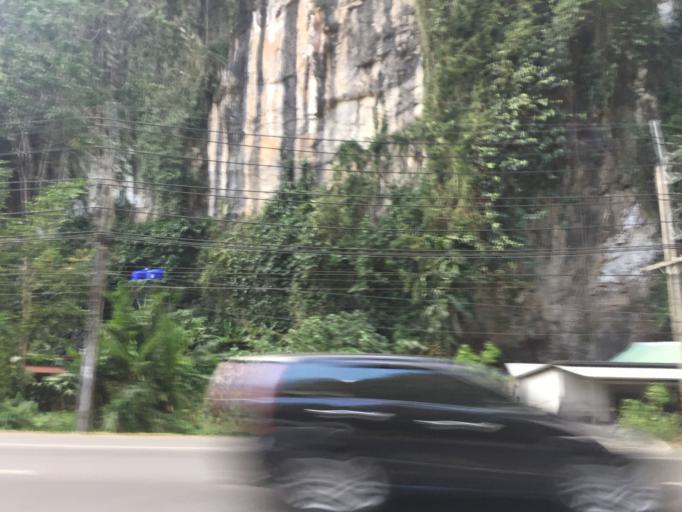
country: TH
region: Phangnga
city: Ban Ao Nang
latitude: 8.0759
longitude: 98.8432
